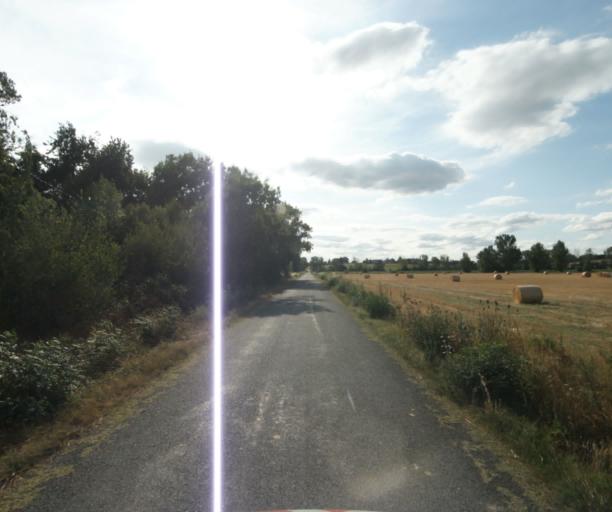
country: FR
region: Midi-Pyrenees
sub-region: Departement du Tarn
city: Puylaurens
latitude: 43.5195
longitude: 1.9979
